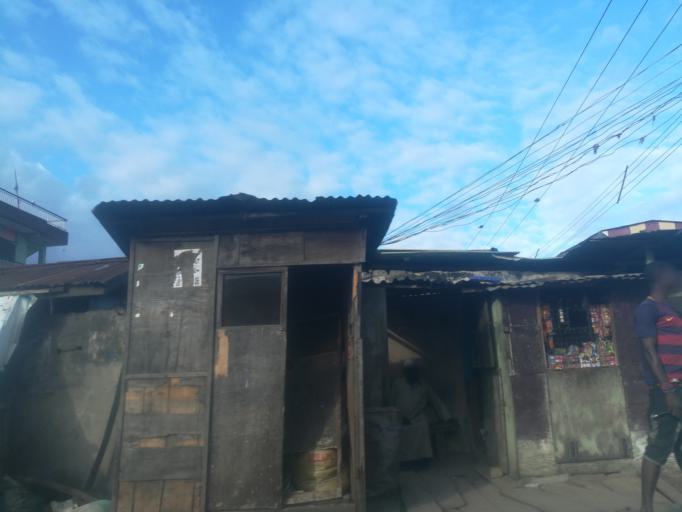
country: NG
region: Lagos
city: Somolu
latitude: 6.5427
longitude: 3.3867
